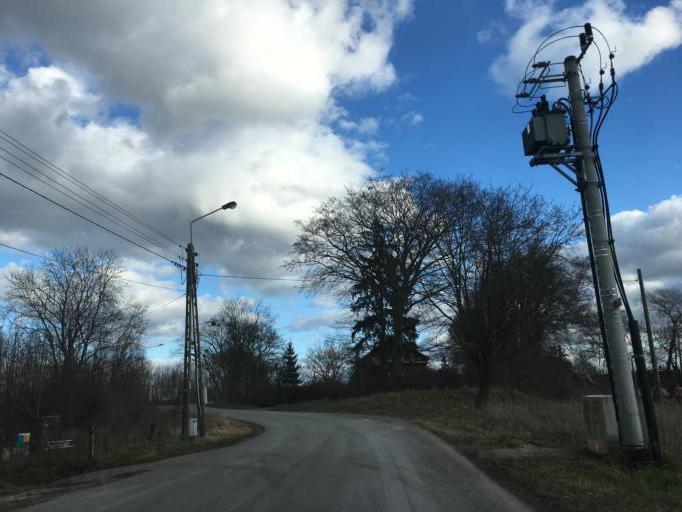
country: PL
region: Pomeranian Voivodeship
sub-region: Powiat gdanski
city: Cedry Wielkie
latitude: 54.3102
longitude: 18.9217
